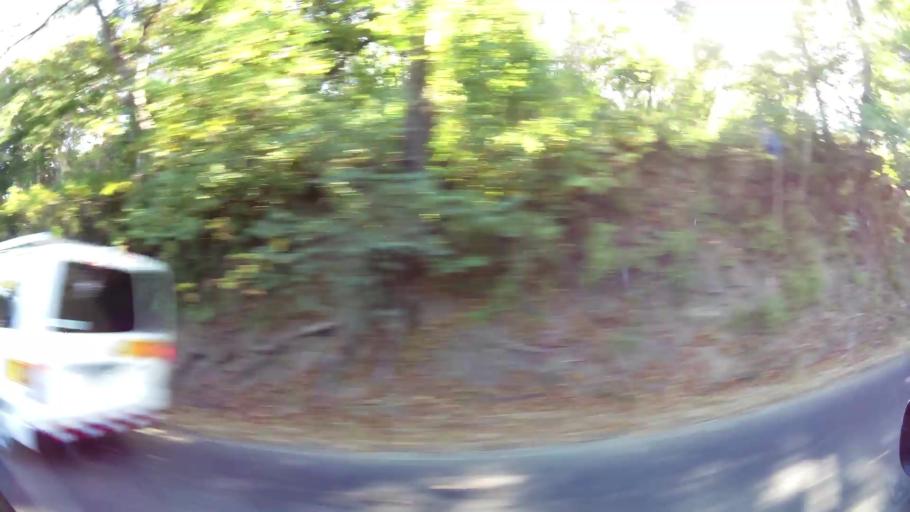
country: CR
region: Guanacaste
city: Belen
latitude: 10.3802
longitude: -85.6210
